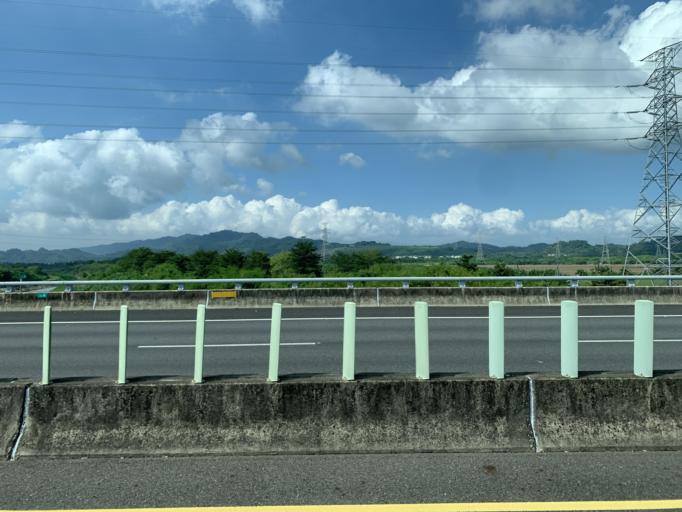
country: TW
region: Taiwan
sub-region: Pingtung
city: Pingtung
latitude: 22.8611
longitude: 120.4916
